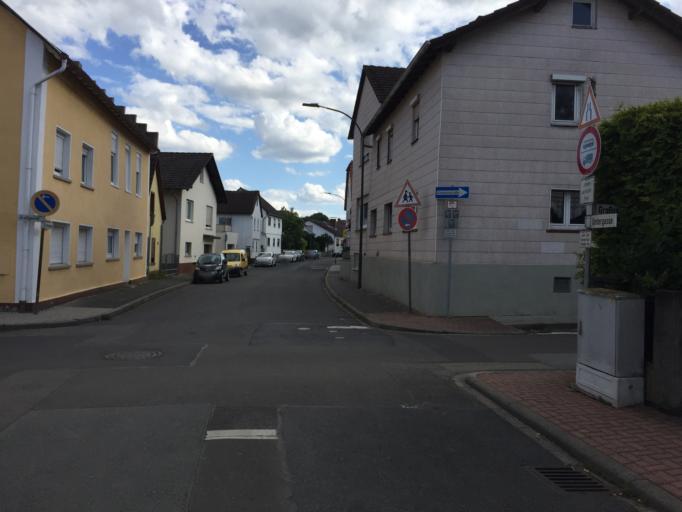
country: DE
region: Hesse
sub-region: Regierungsbezirk Darmstadt
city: Karben
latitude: 50.2503
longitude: 8.7587
